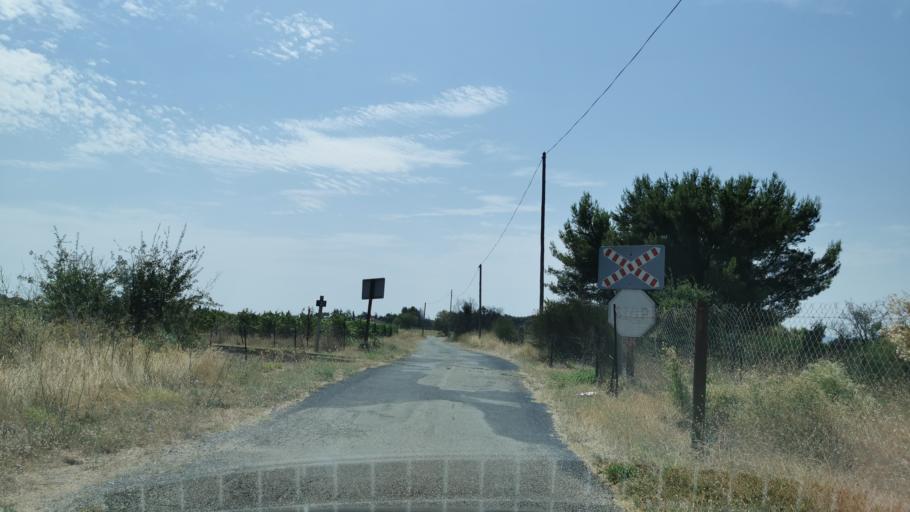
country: FR
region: Languedoc-Roussillon
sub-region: Departement de l'Aude
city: Bize-Minervois
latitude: 43.2981
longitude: 2.8767
